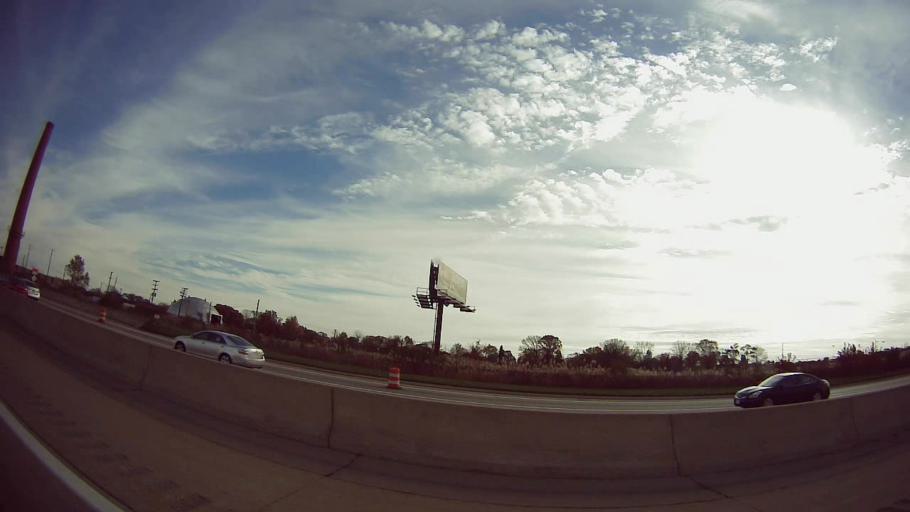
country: US
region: Michigan
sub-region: Wayne County
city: Dearborn Heights
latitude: 42.3780
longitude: -83.2244
